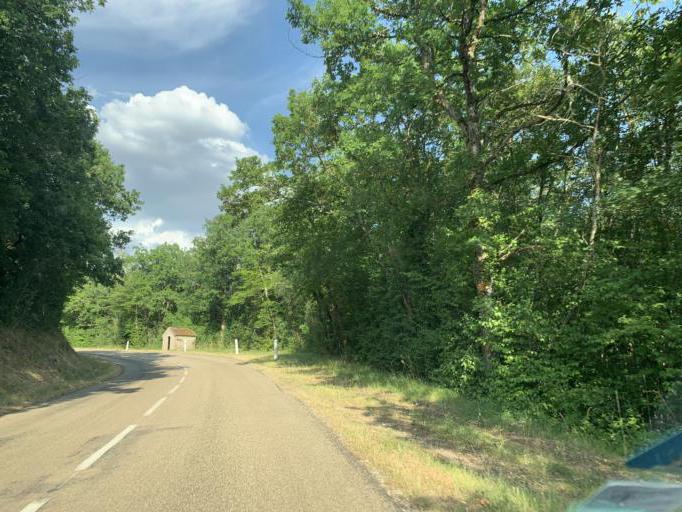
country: FR
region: Bourgogne
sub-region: Departement de l'Yonne
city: Fontenailles
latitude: 47.5331
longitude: 3.4024
